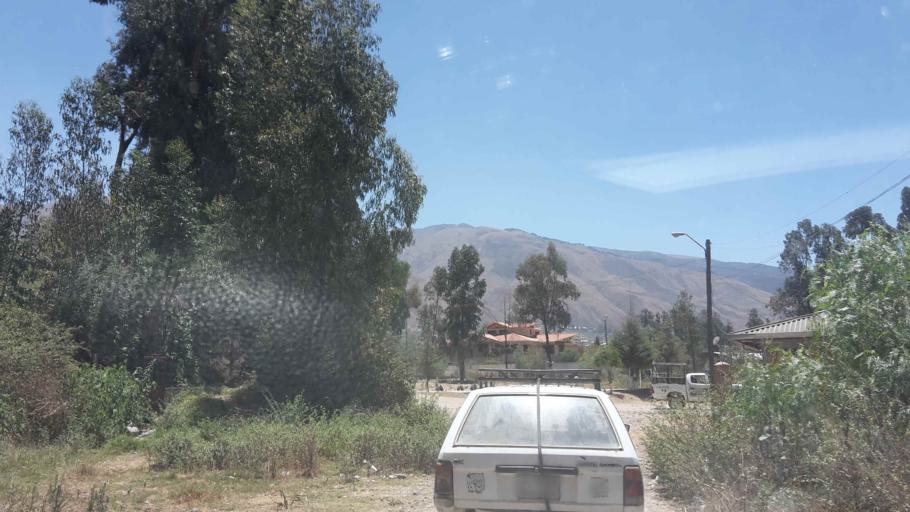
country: BO
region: Cochabamba
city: Cochabamba
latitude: -17.3428
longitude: -66.2145
